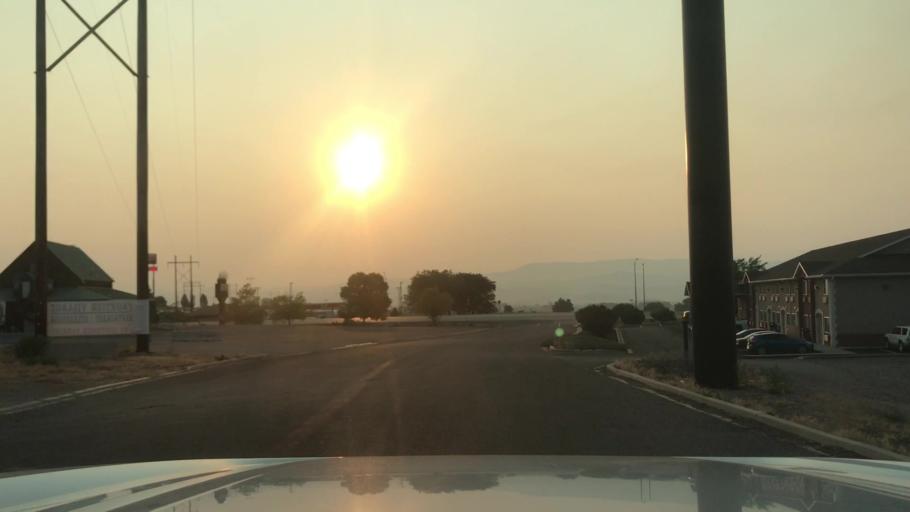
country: US
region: Utah
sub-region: Sevier County
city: Richfield
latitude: 38.7880
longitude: -112.0849
